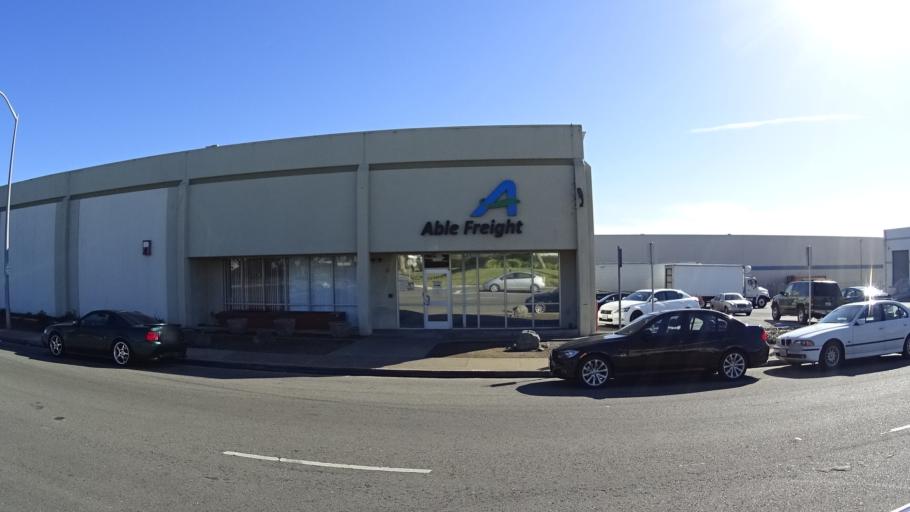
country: US
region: California
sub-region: San Mateo County
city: South San Francisco
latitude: 37.6517
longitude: -122.3904
